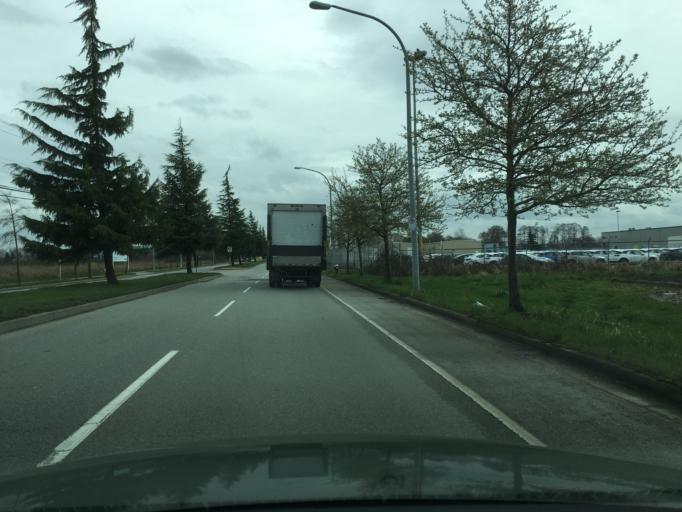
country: CA
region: British Columbia
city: Ladner
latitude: 49.1335
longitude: -123.0730
